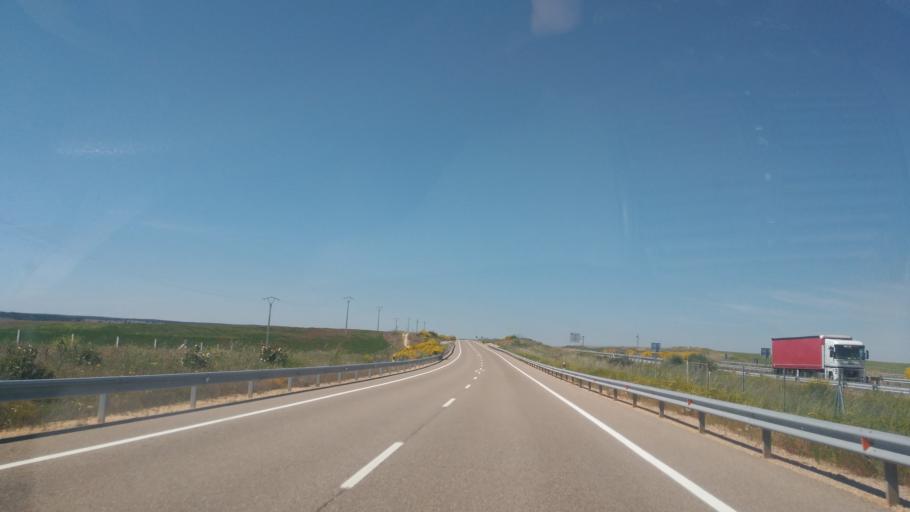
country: ES
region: Castille and Leon
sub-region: Provincia de Salamanca
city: Calzada de Valdunciel
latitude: 41.1131
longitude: -5.6990
